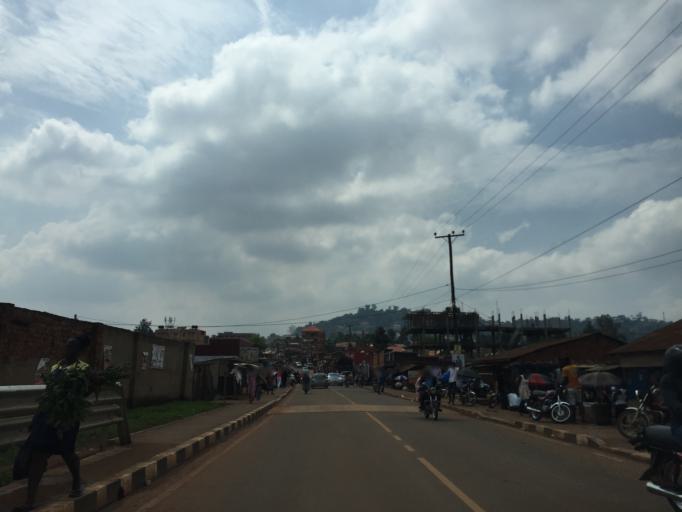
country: UG
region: Central Region
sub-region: Kampala District
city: Kampala
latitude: 0.2887
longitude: 32.5964
